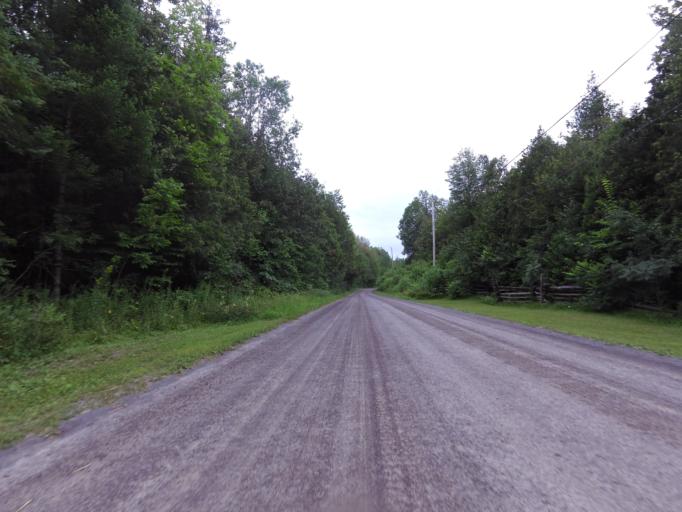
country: CA
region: Ontario
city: Carleton Place
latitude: 45.1509
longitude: -76.2128
